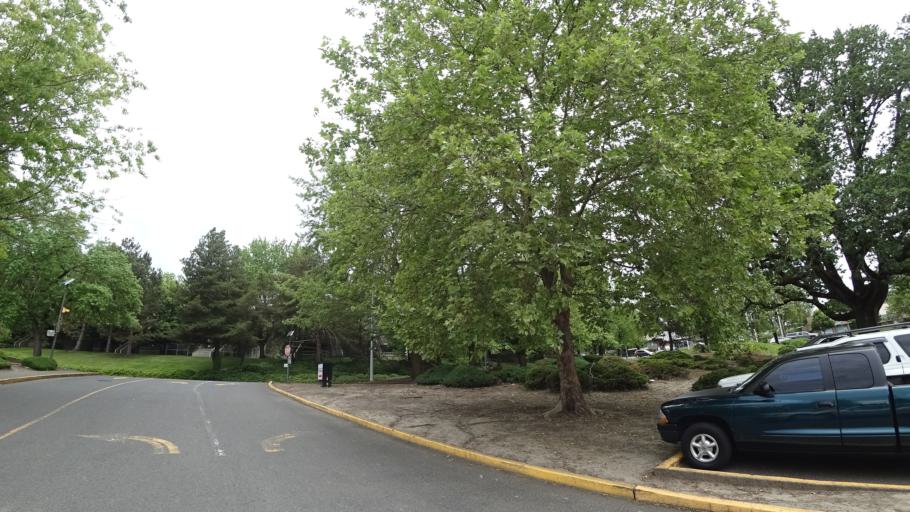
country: US
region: Oregon
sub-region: Washington County
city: Beaverton
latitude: 45.4607
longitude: -122.7971
